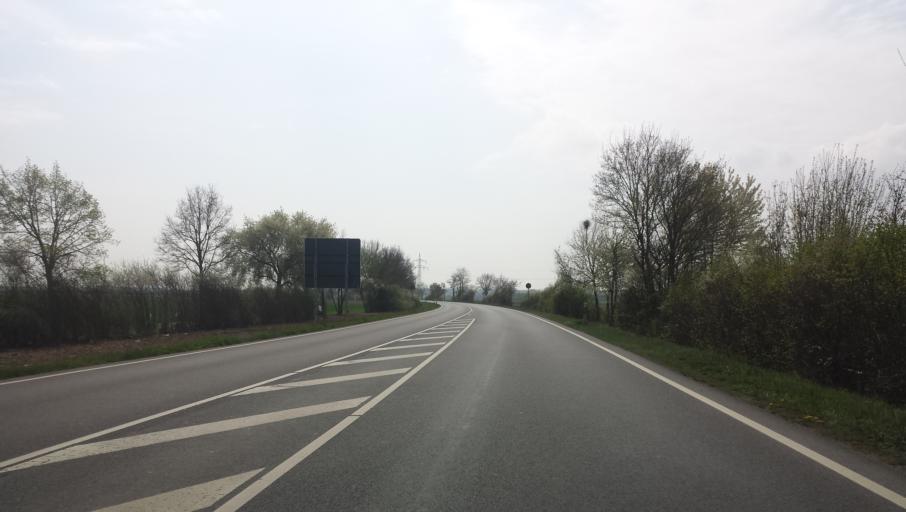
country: DE
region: Hesse
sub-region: Regierungsbezirk Darmstadt
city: Riedstadt
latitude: 49.8538
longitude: 8.4807
